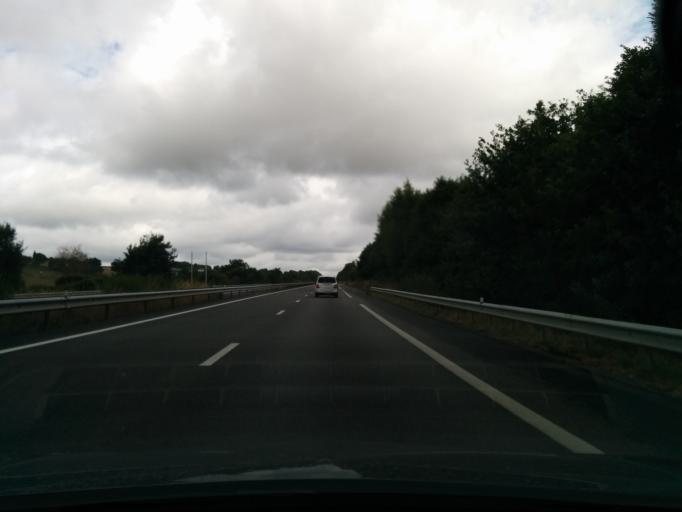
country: FR
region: Limousin
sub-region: Departement de la Correze
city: Vigeois
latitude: 45.4307
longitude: 1.5126
